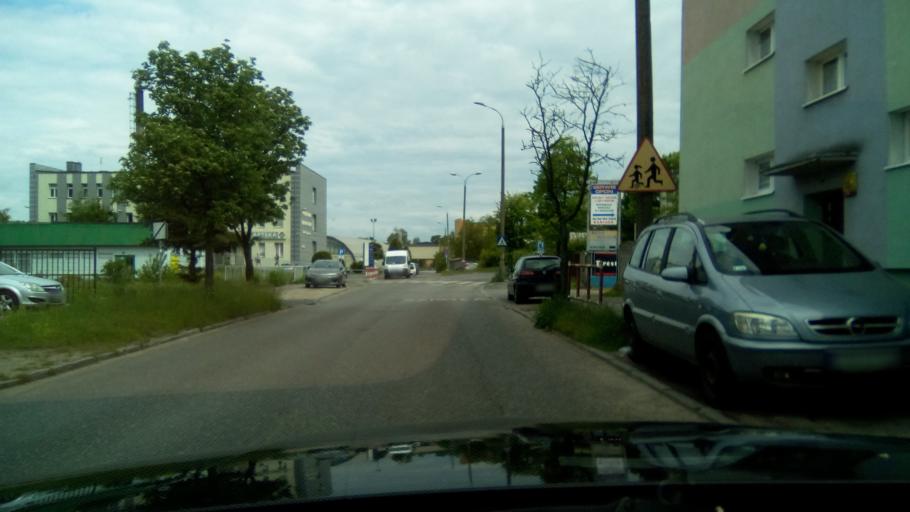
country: PL
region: Greater Poland Voivodeship
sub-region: Powiat gnieznienski
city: Gniezno
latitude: 52.5184
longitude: 17.5989
